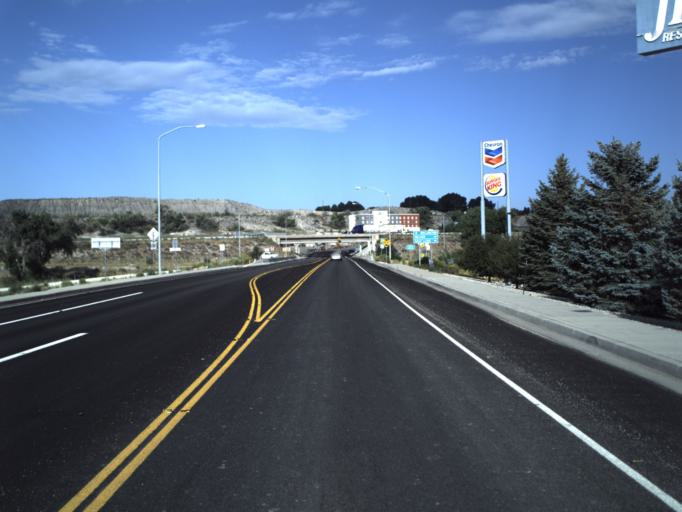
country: US
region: Utah
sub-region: Carbon County
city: Price
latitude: 39.6009
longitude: -110.8235
